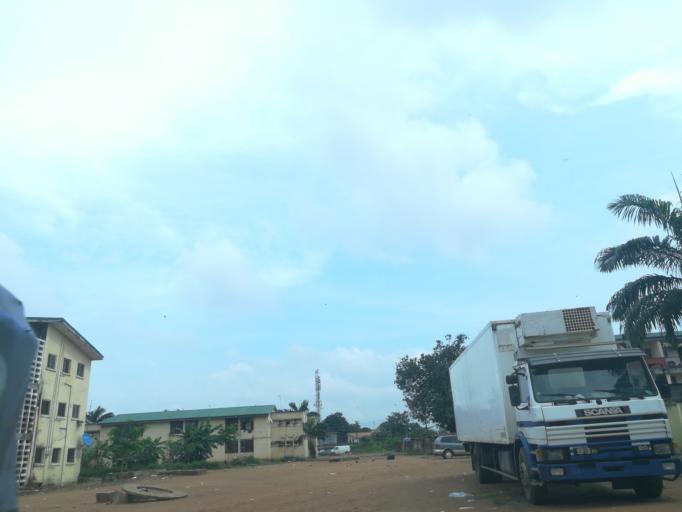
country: NG
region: Lagos
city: Oshodi
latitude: 6.5697
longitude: 3.3558
